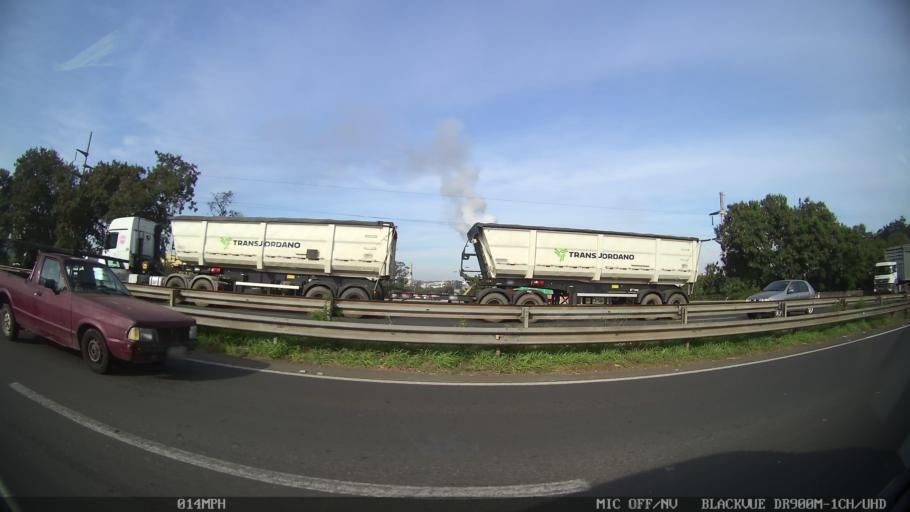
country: BR
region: Sao Paulo
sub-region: Piracicaba
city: Piracicaba
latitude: -22.6861
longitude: -47.6725
